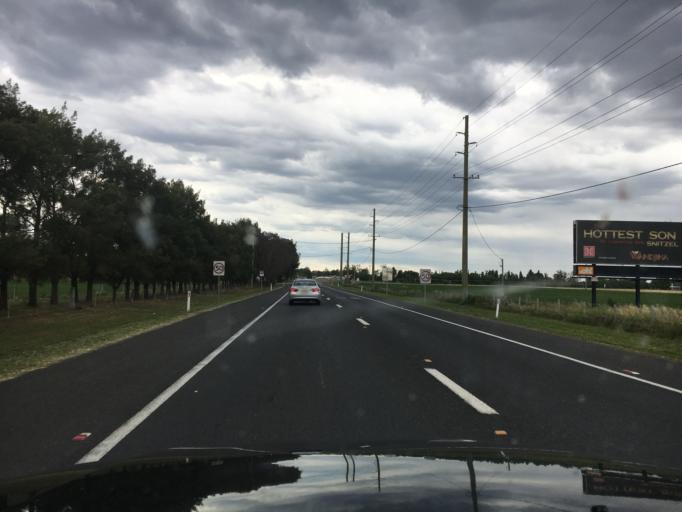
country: AU
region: New South Wales
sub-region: Muswellbrook
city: Muswellbrook
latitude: -32.1514
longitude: 150.8842
